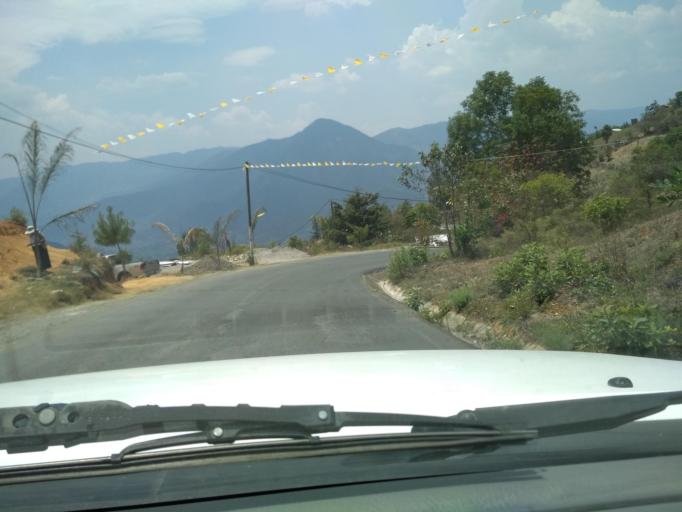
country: MX
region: Veracruz
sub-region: Acultzingo
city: Acatla
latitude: 18.7487
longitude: -97.1920
